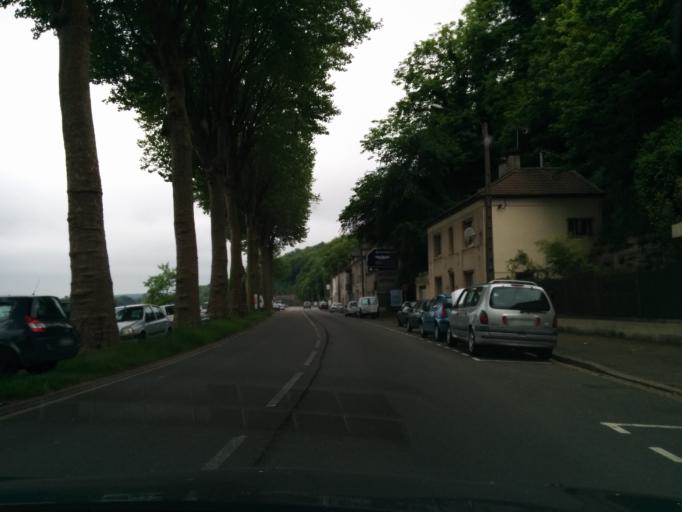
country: FR
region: Ile-de-France
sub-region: Departement des Yvelines
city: Rosny-sur-Seine
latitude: 49.0168
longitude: 1.6107
